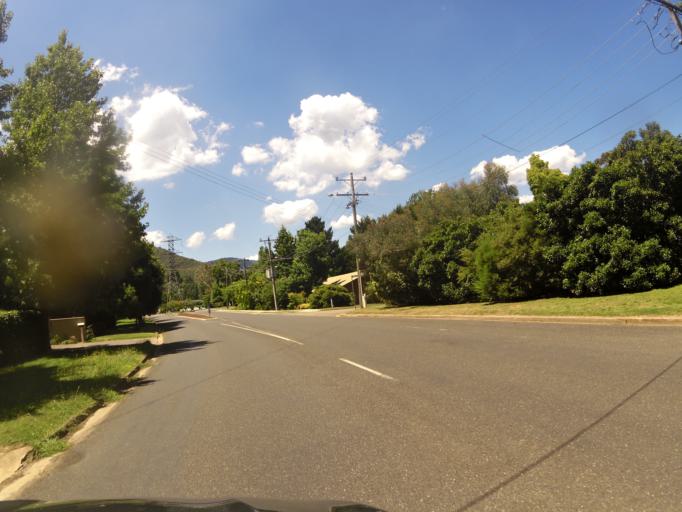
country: AU
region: Victoria
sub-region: Alpine
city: Mount Beauty
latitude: -36.7260
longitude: 146.9560
